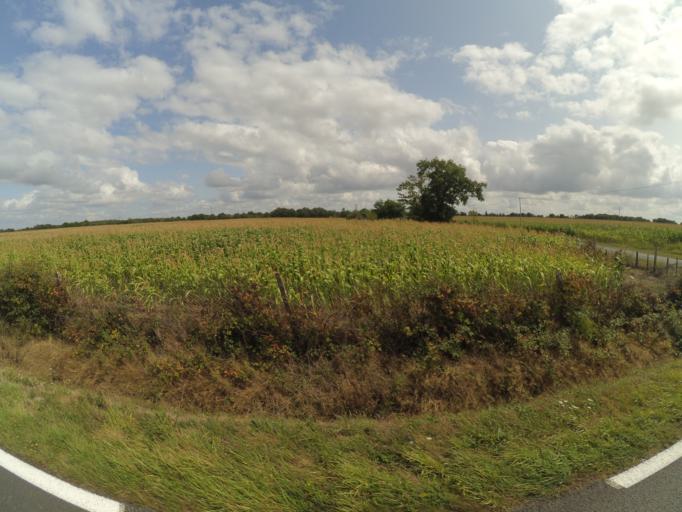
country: FR
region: Pays de la Loire
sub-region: Departement de la Vendee
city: La Bernardiere
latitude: 47.0172
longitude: -1.2744
